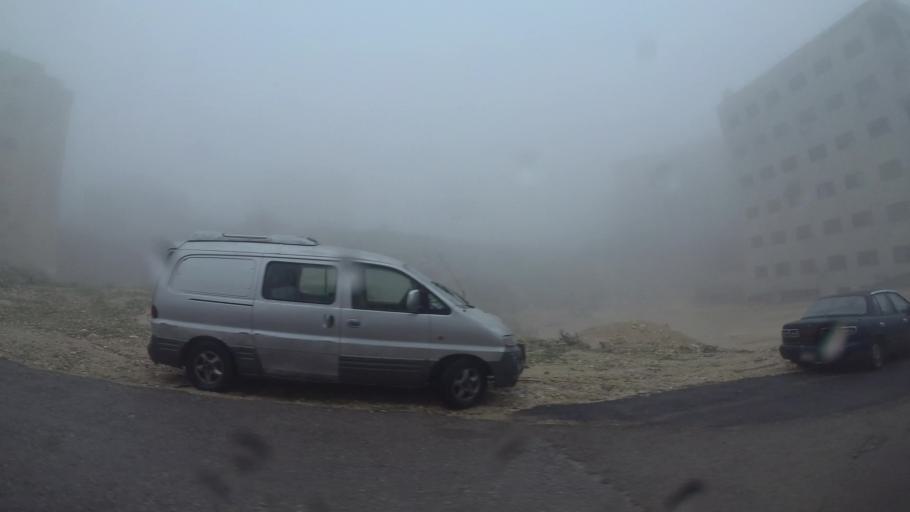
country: JO
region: Amman
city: Al Jubayhah
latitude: 32.0042
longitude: 35.8903
